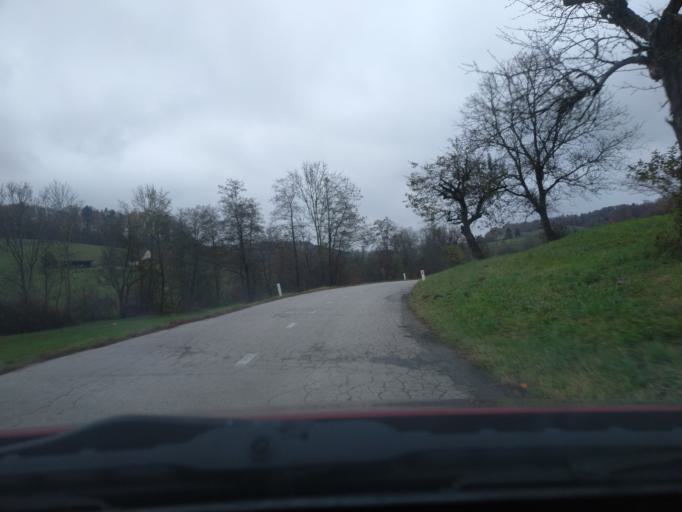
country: SI
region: Kungota
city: Zgornja Kungota
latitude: 46.6529
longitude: 15.6128
